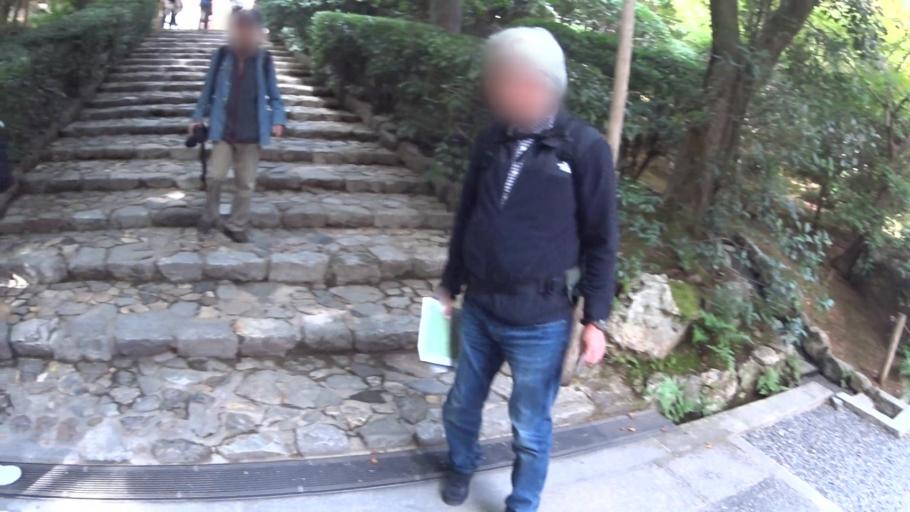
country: JP
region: Kyoto
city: Kyoto
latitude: 35.0347
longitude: 135.7186
